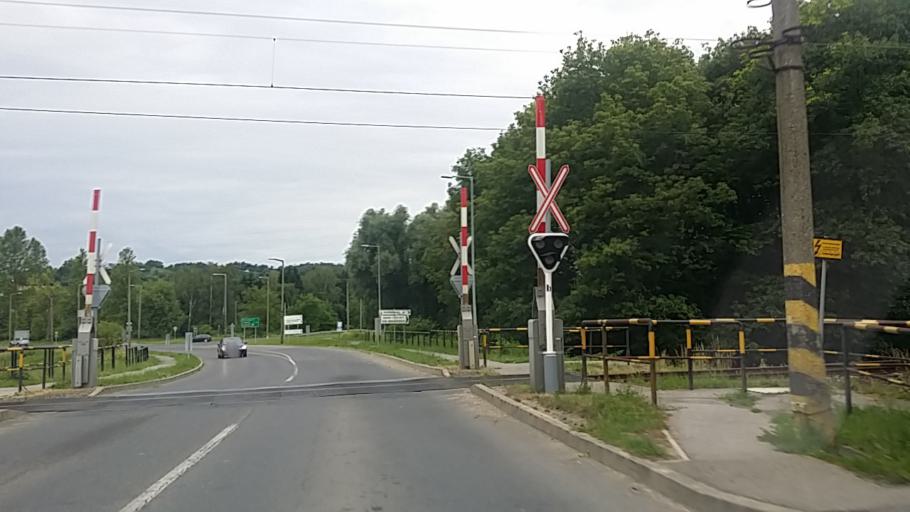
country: HU
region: Zala
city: Zalaegerszeg
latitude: 46.8584
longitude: 16.8011
